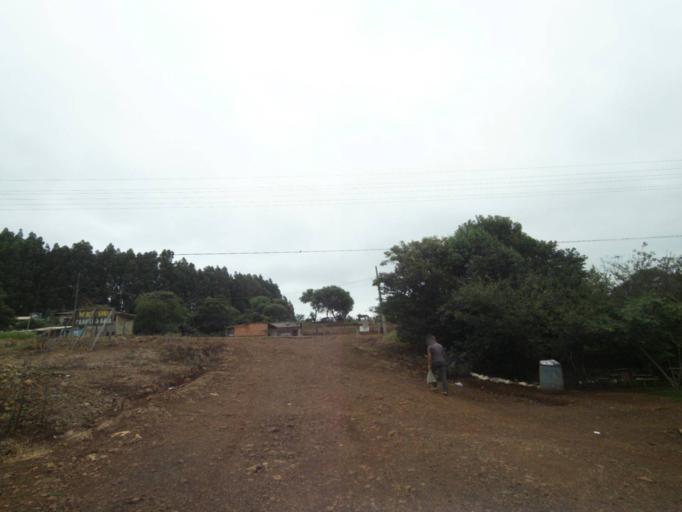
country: BR
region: Parana
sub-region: Pitanga
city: Pitanga
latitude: -24.9291
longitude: -51.8745
